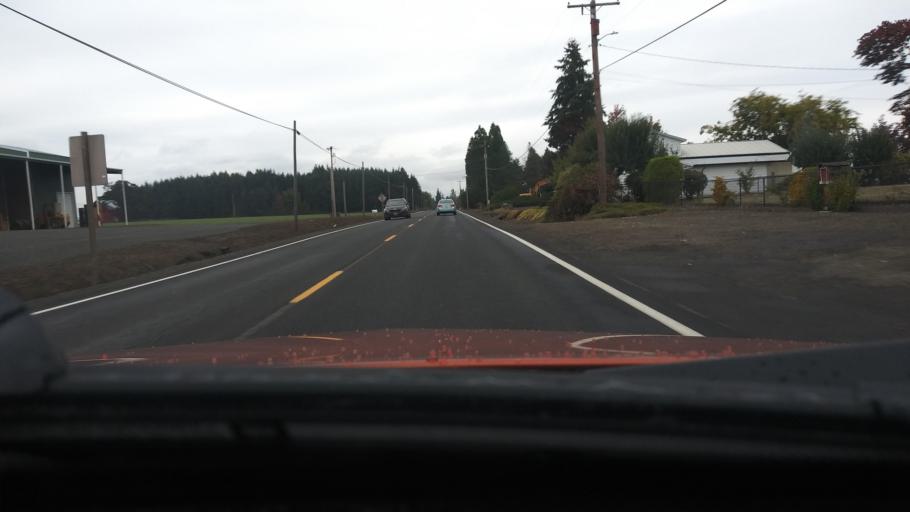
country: US
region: Oregon
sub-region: Washington County
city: Forest Grove
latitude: 45.5530
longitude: -123.1058
